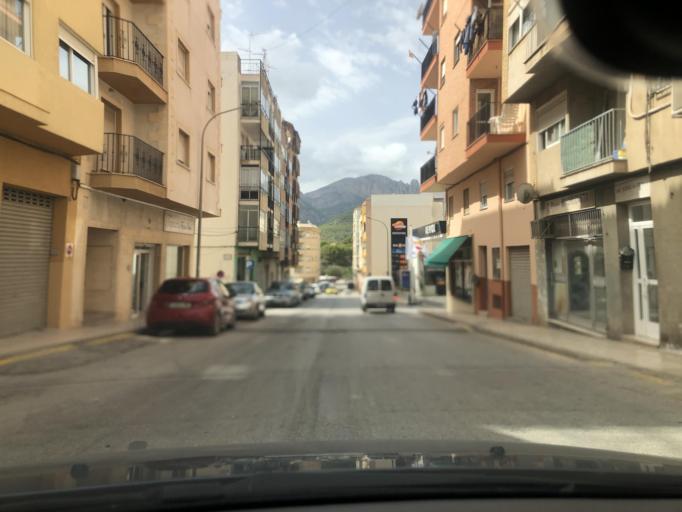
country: ES
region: Valencia
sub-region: Provincia de Alicante
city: Callosa d'En Sarria
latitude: 38.6480
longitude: -0.1201
